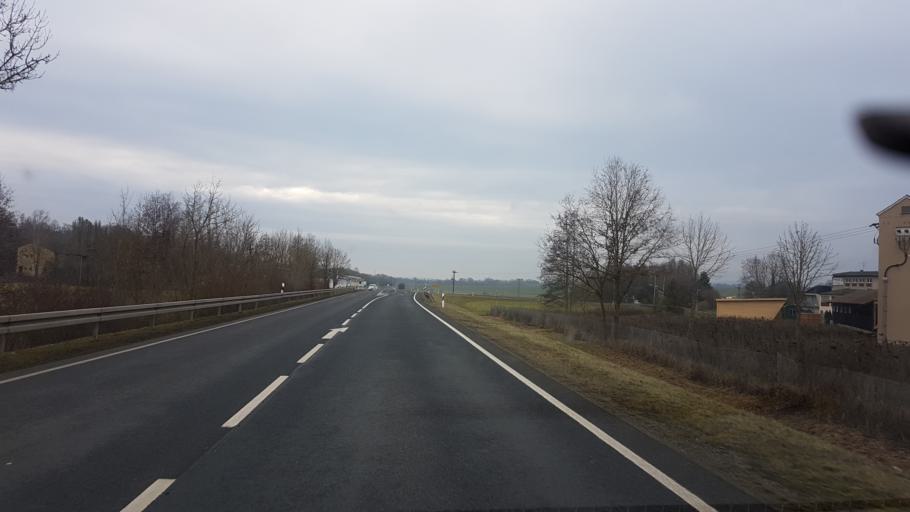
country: DE
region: Bavaria
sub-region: Regierungsbezirk Unterfranken
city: Ermershausen
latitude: 50.2411
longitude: 10.5691
